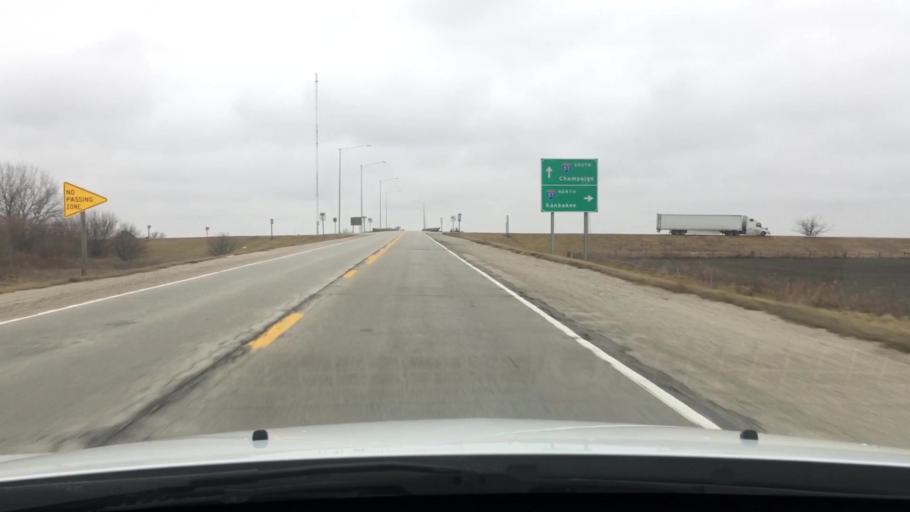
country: US
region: Illinois
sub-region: Iroquois County
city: Clifton
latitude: 40.8842
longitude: -87.9632
